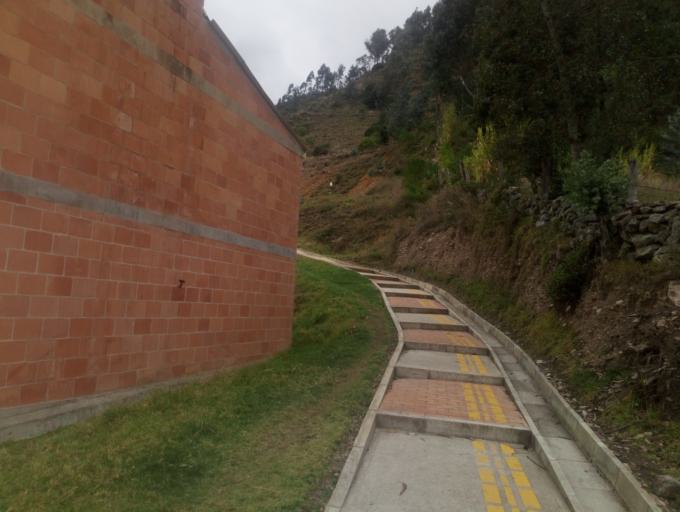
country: CO
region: Boyaca
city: Susacon
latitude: 6.1292
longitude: -72.7101
